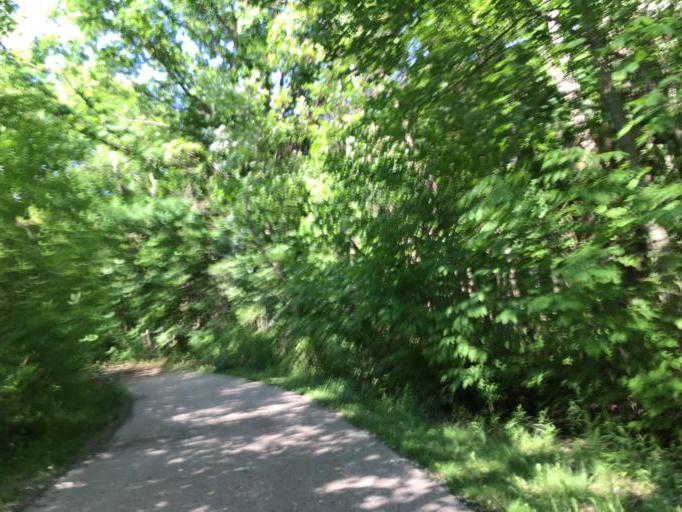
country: US
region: Michigan
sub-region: Oakland County
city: South Lyon
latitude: 42.4386
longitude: -83.6600
